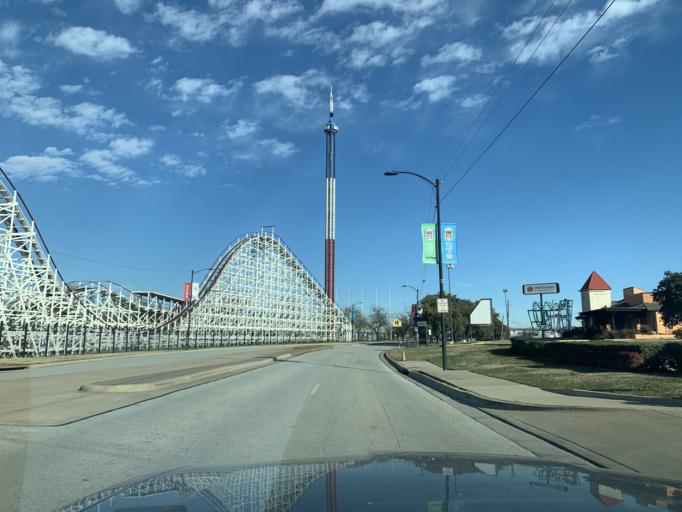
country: US
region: Texas
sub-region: Tarrant County
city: Arlington
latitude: 32.7545
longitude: -97.0672
